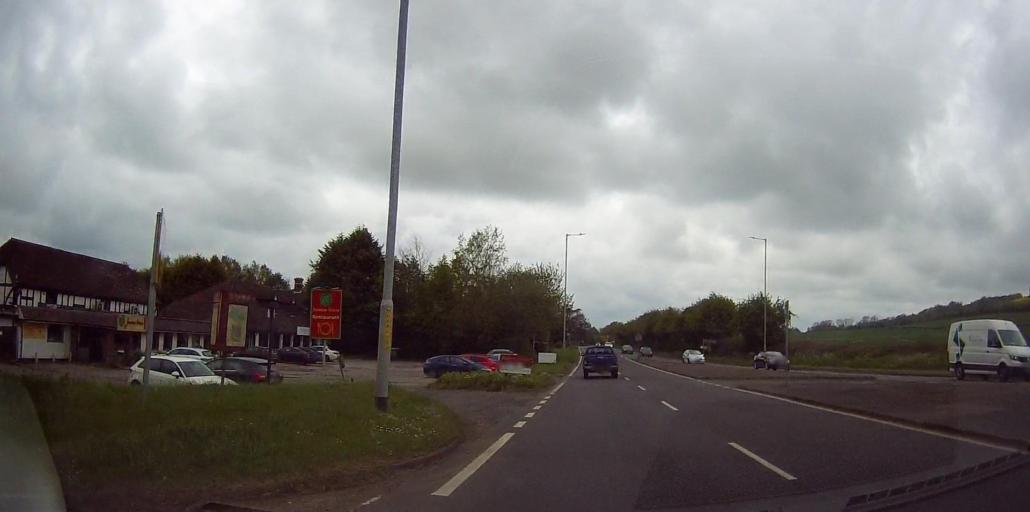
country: GB
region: England
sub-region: Kent
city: Lenham
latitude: 51.2133
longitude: 0.7892
